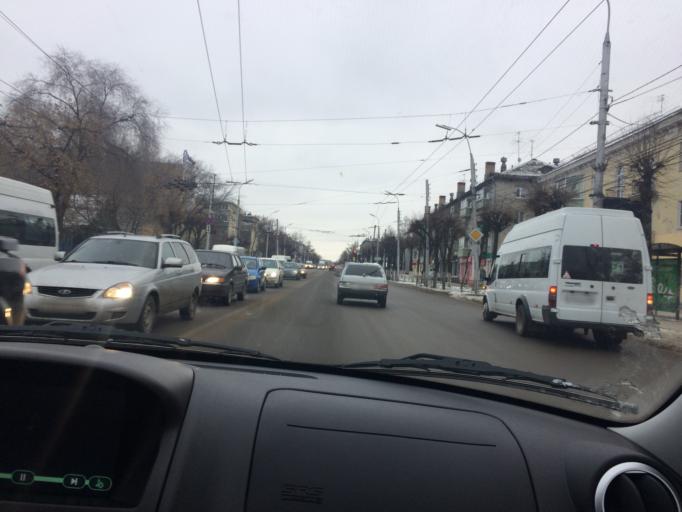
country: RU
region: Rjazan
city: Ryazan'
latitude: 54.6247
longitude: 39.7171
